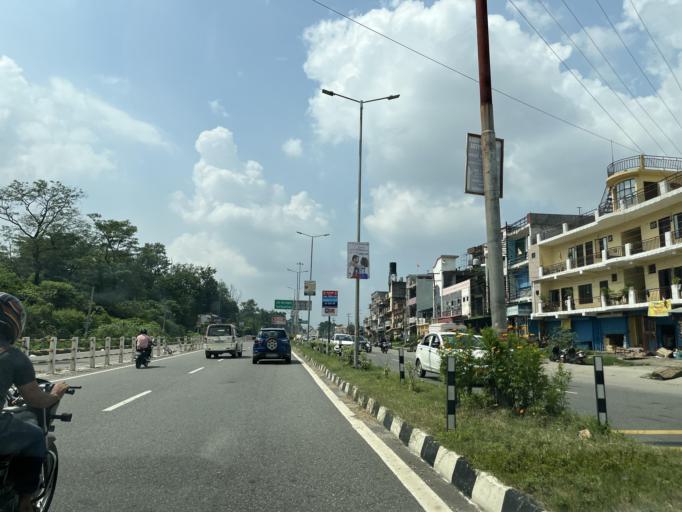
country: IN
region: Uttarakhand
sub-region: Dehradun
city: Raipur
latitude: 30.2715
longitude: 78.0790
